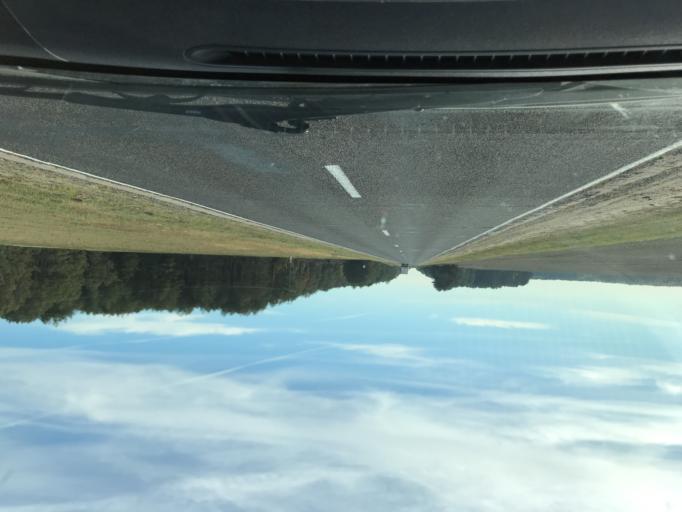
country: BY
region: Brest
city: Lahishyn
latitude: 52.1537
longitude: 25.8107
